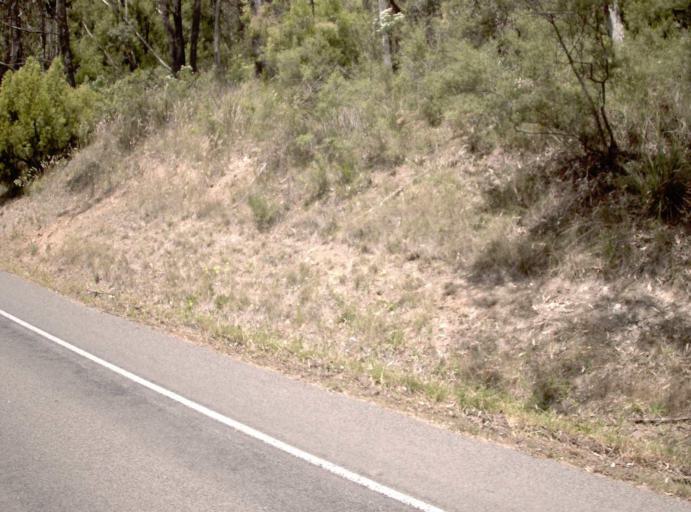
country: AU
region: Victoria
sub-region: Latrobe
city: Traralgon
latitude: -38.3797
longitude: 146.7568
